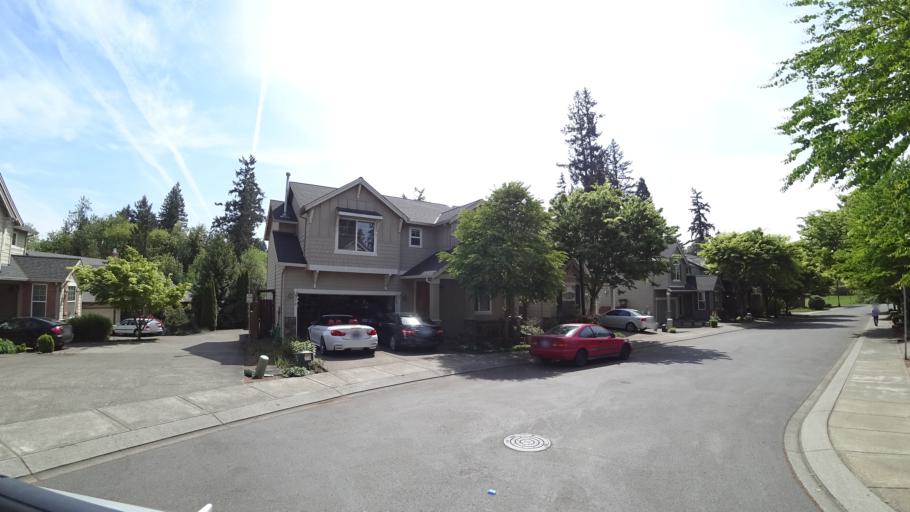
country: US
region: Oregon
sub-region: Washington County
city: Hillsboro
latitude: 45.5223
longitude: -122.9348
